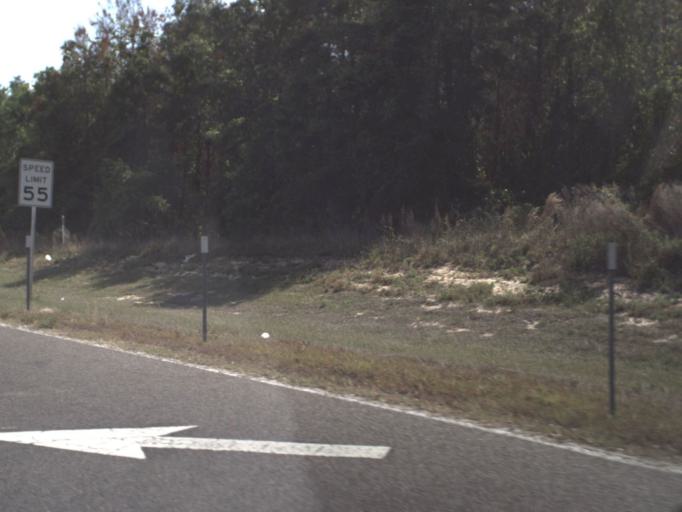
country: US
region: Florida
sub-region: Lake County
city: Hawthorne
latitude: 28.7452
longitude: -81.8762
